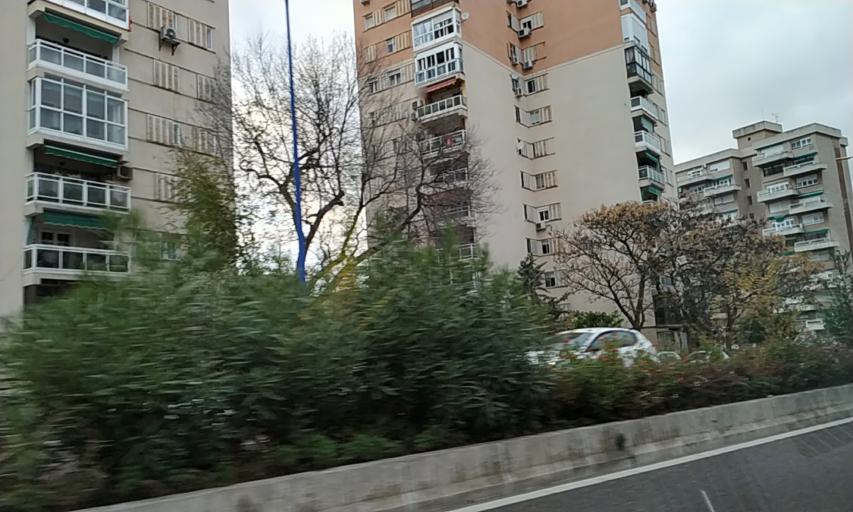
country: ES
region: Extremadura
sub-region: Provincia de Badajoz
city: Badajoz
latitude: 38.8747
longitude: -6.9813
